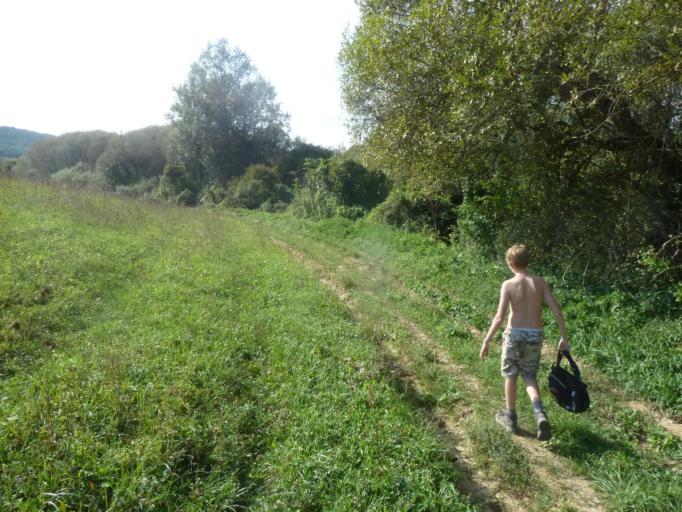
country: HU
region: Nograd
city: Romhany
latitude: 47.8689
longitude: 19.2655
